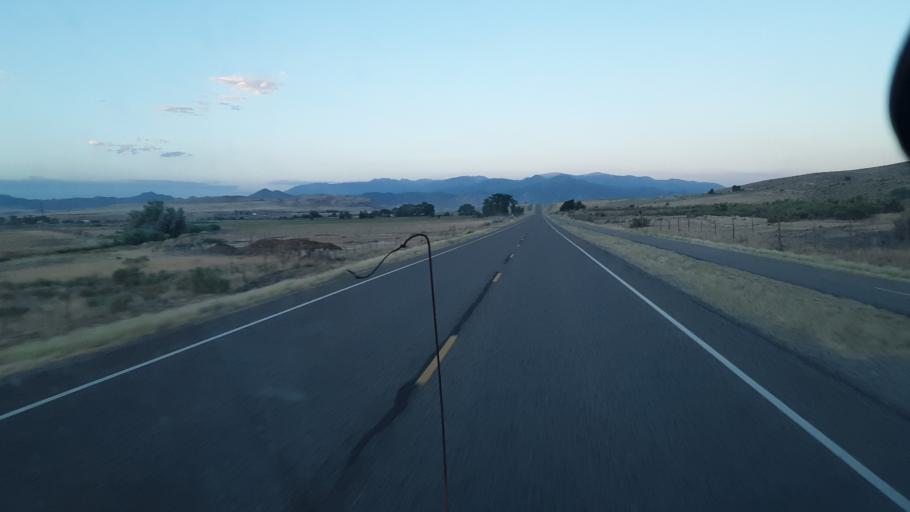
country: US
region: Utah
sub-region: Sevier County
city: Monroe
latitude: 38.6700
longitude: -112.1669
